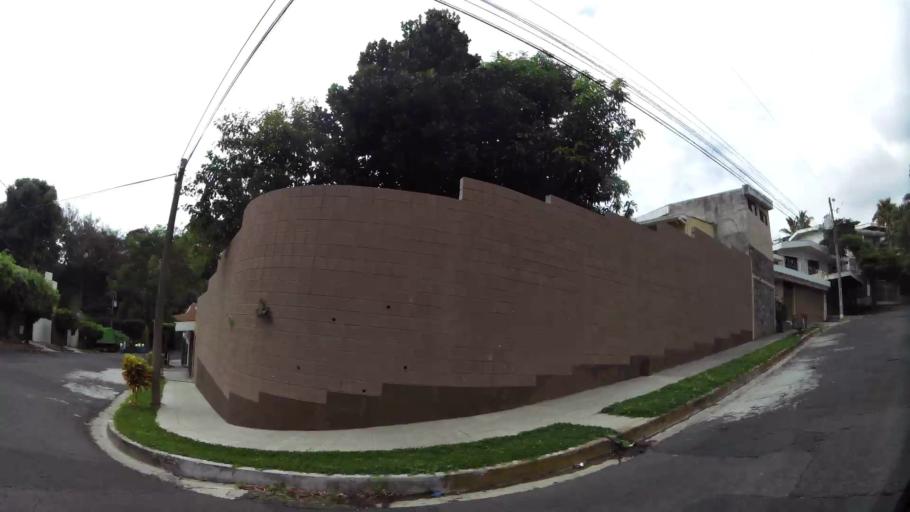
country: SV
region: La Libertad
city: Santa Tecla
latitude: 13.7076
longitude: -89.2567
